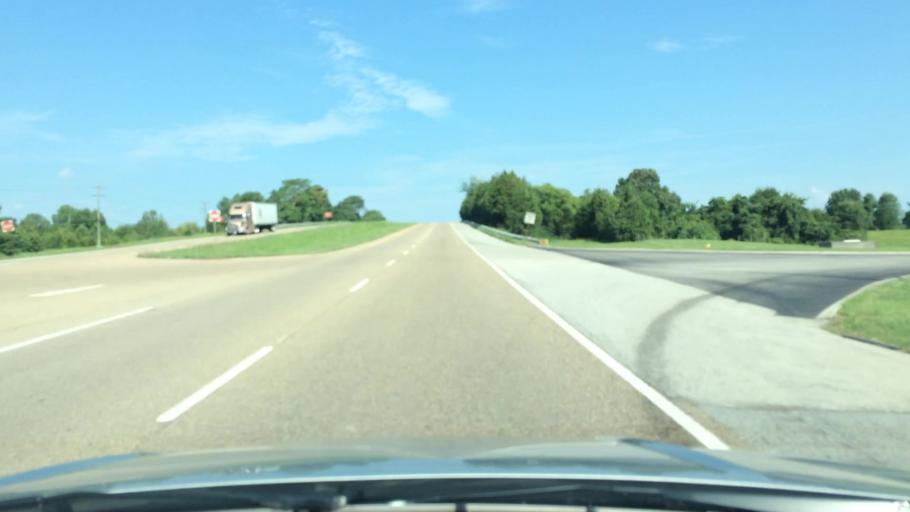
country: US
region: Tennessee
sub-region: Hamblen County
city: Morristown
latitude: 36.1684
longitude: -83.3806
